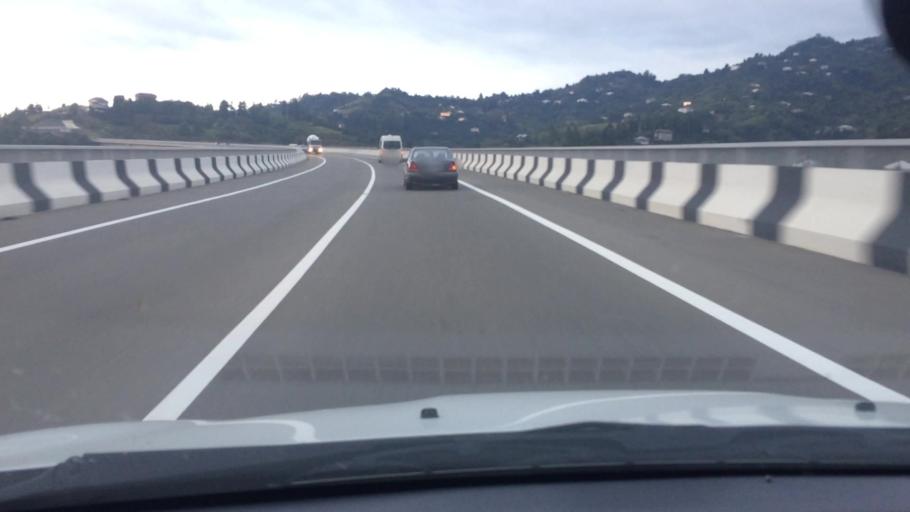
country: GE
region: Ajaria
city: Makhinjauri
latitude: 41.7134
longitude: 41.7522
